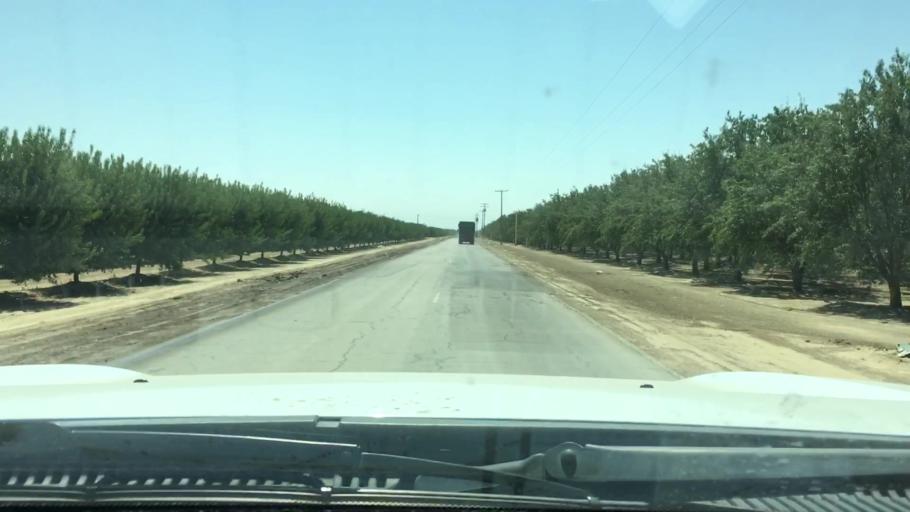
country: US
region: California
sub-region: Kern County
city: Wasco
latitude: 35.5210
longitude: -119.4032
